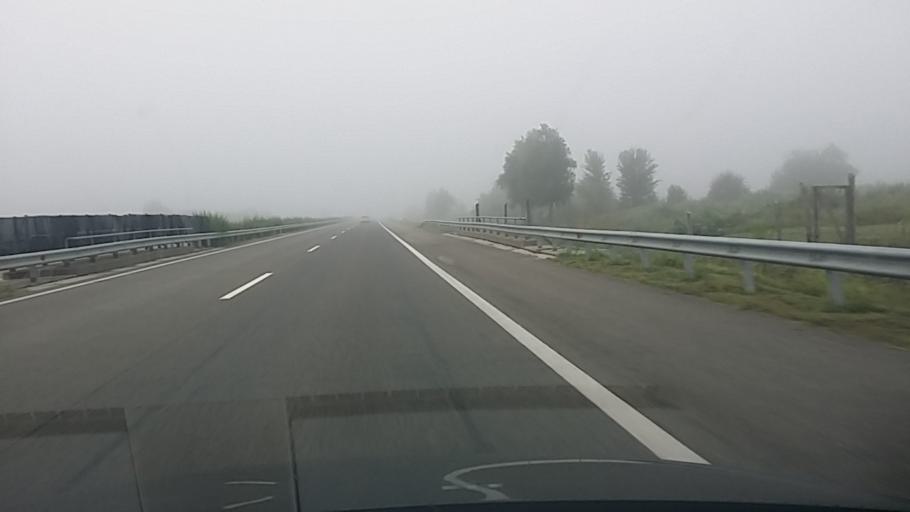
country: HU
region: Csongrad
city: Szatymaz
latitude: 46.2925
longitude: 20.0424
